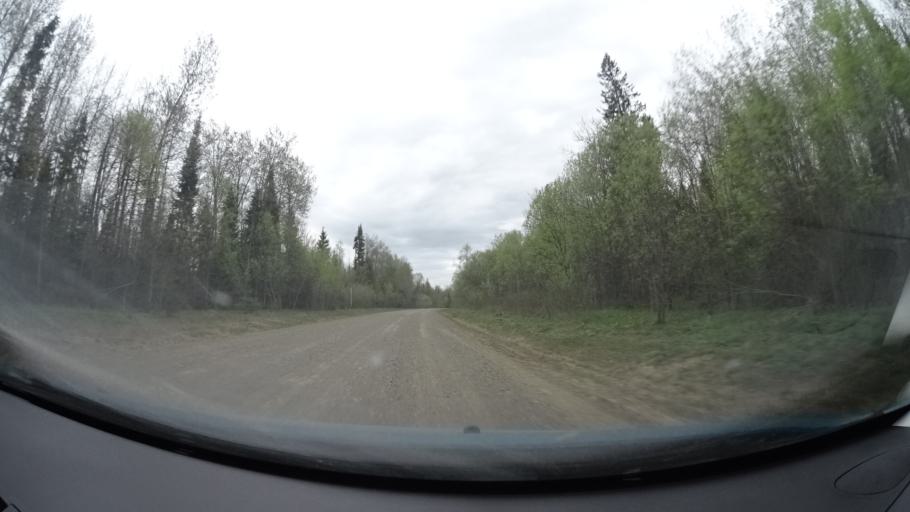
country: RU
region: Perm
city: Kuyeda
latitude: 56.5945
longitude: 55.7057
